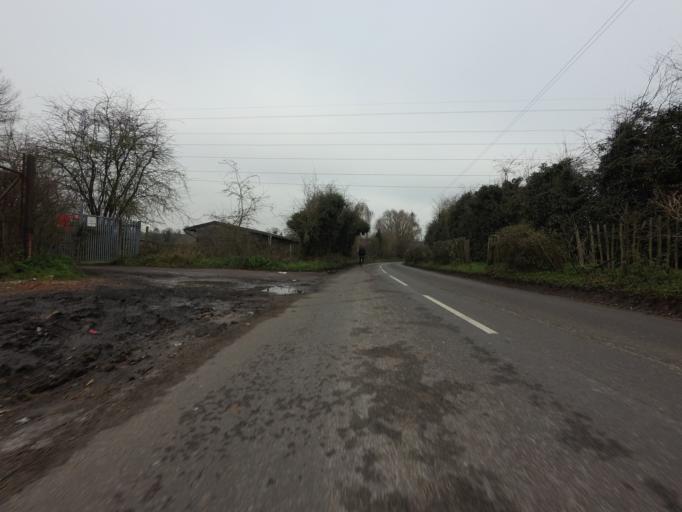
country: GB
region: England
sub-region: Kent
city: Eynsford
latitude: 51.3982
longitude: 0.2455
